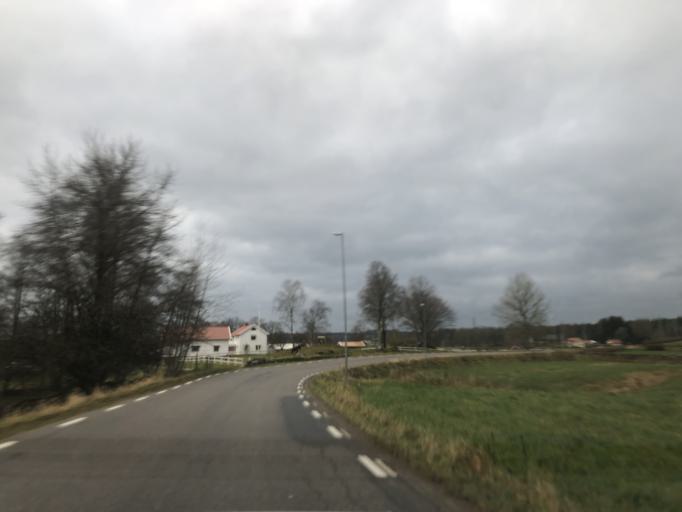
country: SE
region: Vaestra Goetaland
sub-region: Boras Kommun
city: Dalsjofors
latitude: 57.8271
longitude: 13.1779
